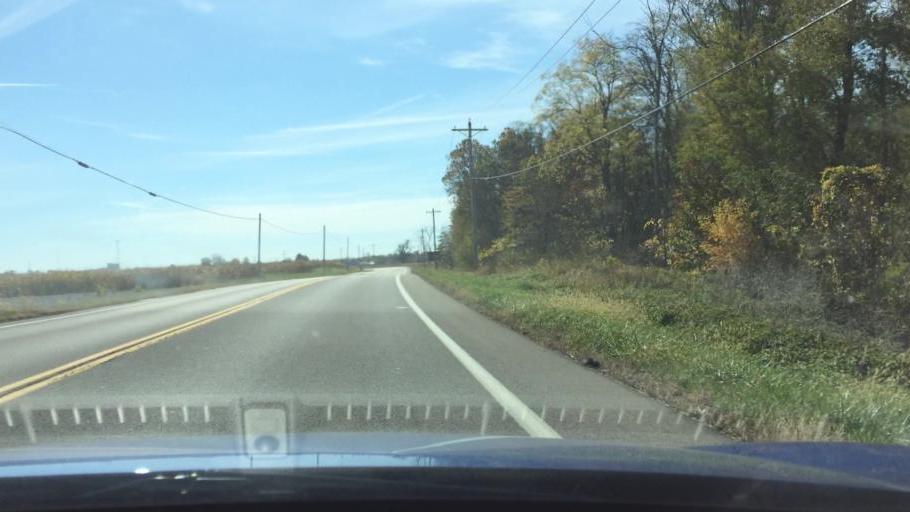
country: US
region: Ohio
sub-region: Logan County
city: Russells Point
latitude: 40.4457
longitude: -83.9048
